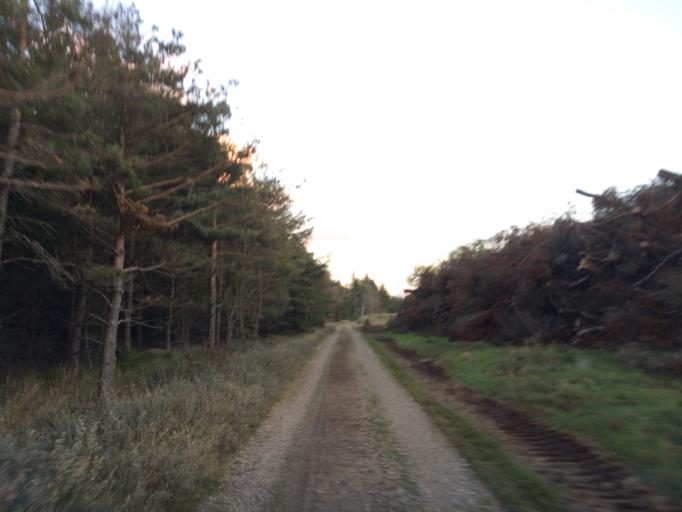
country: DK
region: Central Jutland
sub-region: Holstebro Kommune
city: Ulfborg
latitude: 56.3001
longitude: 8.1452
